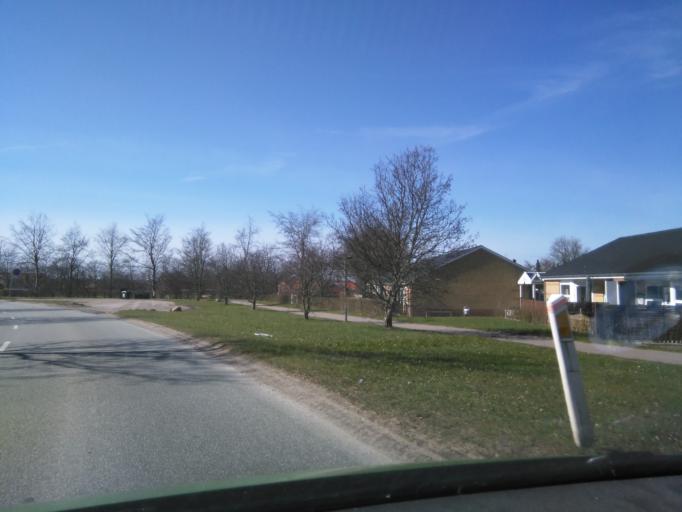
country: DK
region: Central Jutland
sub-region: Arhus Kommune
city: Trige
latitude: 56.2519
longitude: 10.1430
